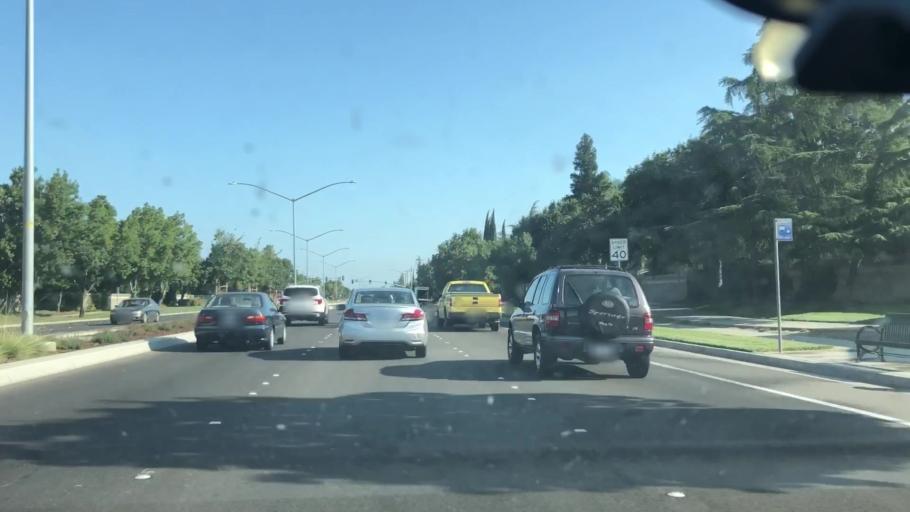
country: US
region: California
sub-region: San Joaquin County
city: Tracy
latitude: 37.7449
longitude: -121.4531
